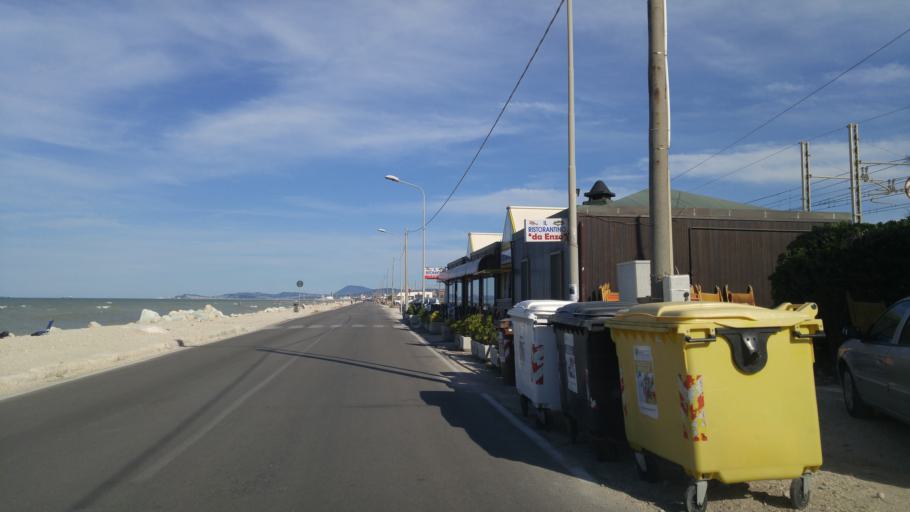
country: IT
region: The Marches
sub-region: Provincia di Ancona
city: Marina di Montemarciano
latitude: 43.6619
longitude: 13.3217
